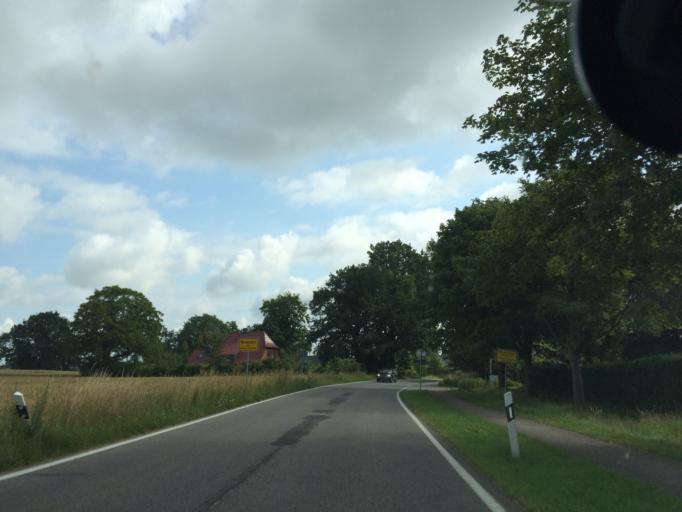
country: DE
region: Schleswig-Holstein
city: Lindau
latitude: 54.3946
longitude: 9.9288
